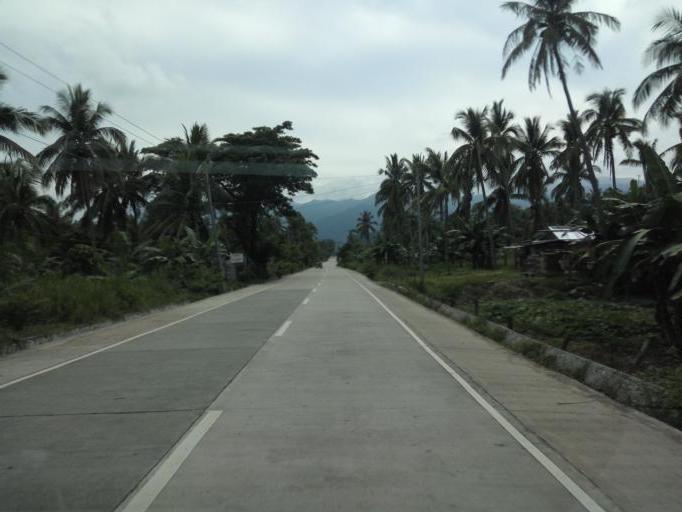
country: PH
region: Central Luzon
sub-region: Province of Aurora
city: Dinalongan
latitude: 16.0774
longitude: 121.7765
